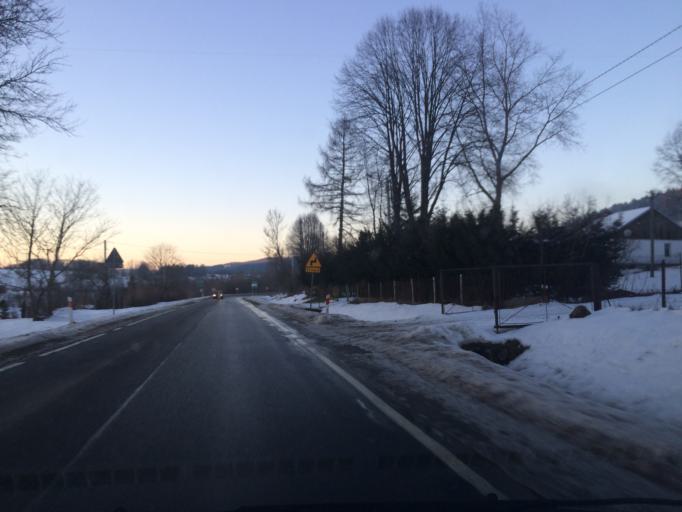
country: PL
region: Subcarpathian Voivodeship
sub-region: Powiat bieszczadzki
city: Czarna
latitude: 49.3783
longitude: 22.6427
